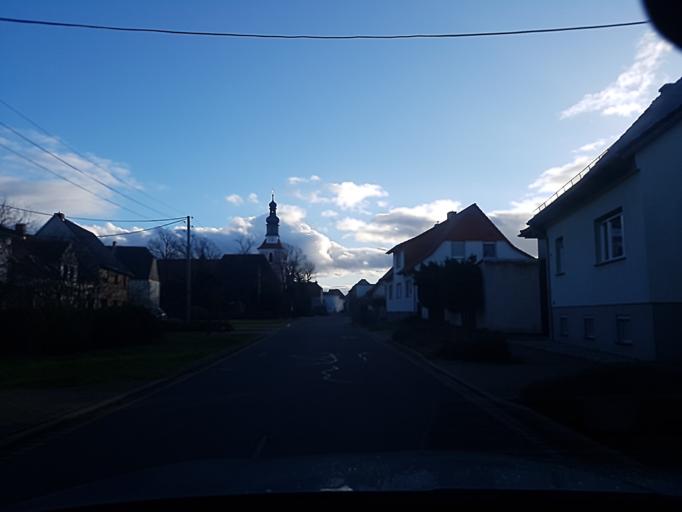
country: DE
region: Brandenburg
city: Bad Liebenwerda
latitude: 51.5521
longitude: 13.3631
